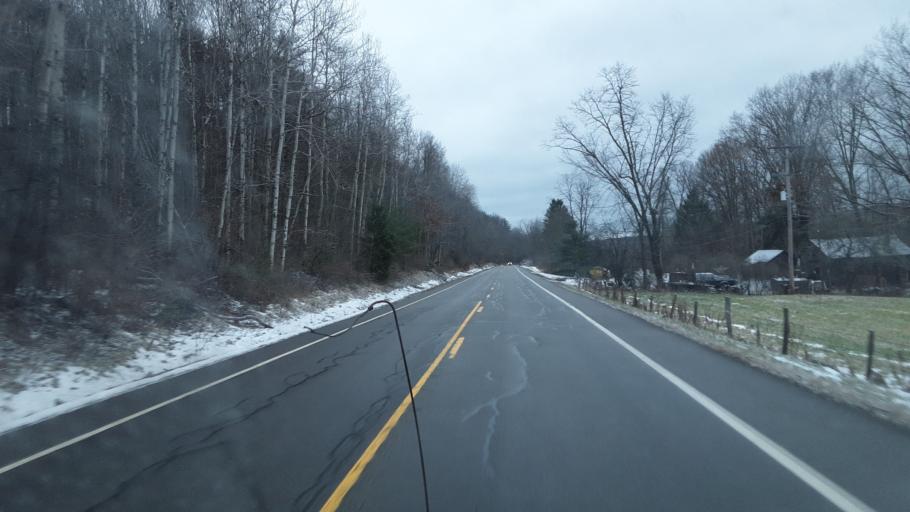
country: US
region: New York
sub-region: Allegany County
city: Belmont
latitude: 42.3165
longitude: -78.0978
